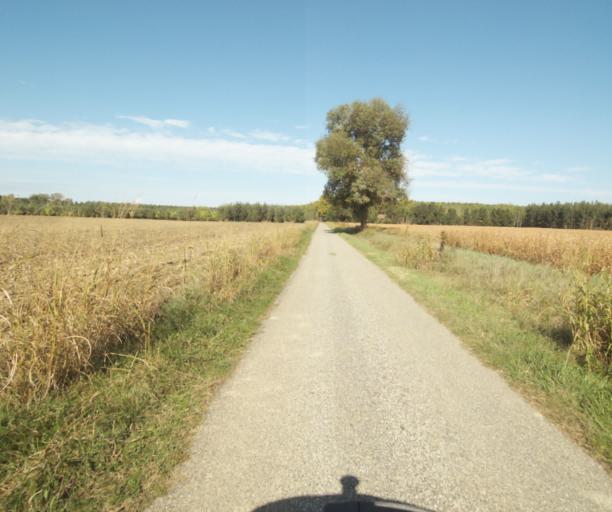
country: FR
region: Midi-Pyrenees
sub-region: Departement du Tarn-et-Garonne
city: Finhan
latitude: 43.8982
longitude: 1.2191
